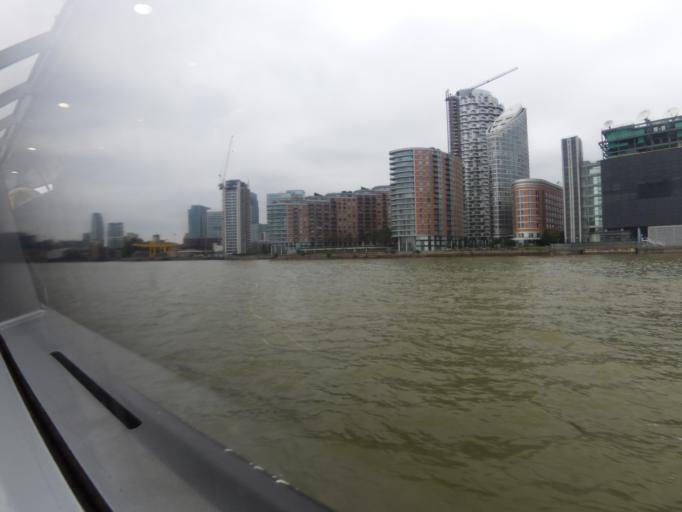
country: GB
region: England
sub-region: Greater London
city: Poplar
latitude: 51.5056
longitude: -0.0016
